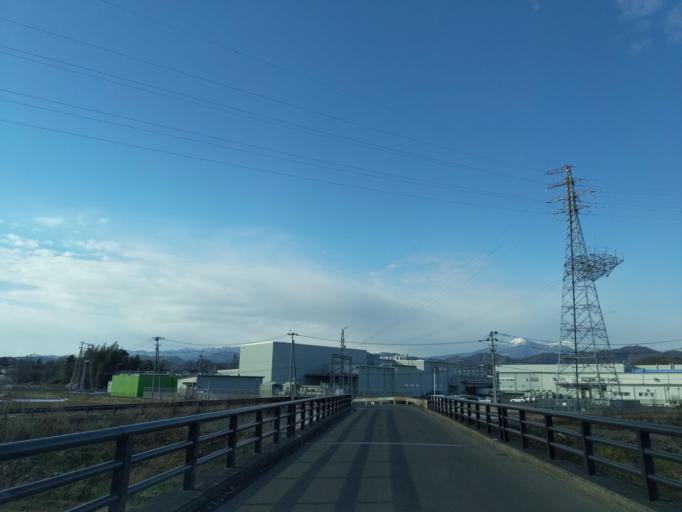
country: JP
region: Fukushima
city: Motomiya
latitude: 37.4736
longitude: 140.3725
